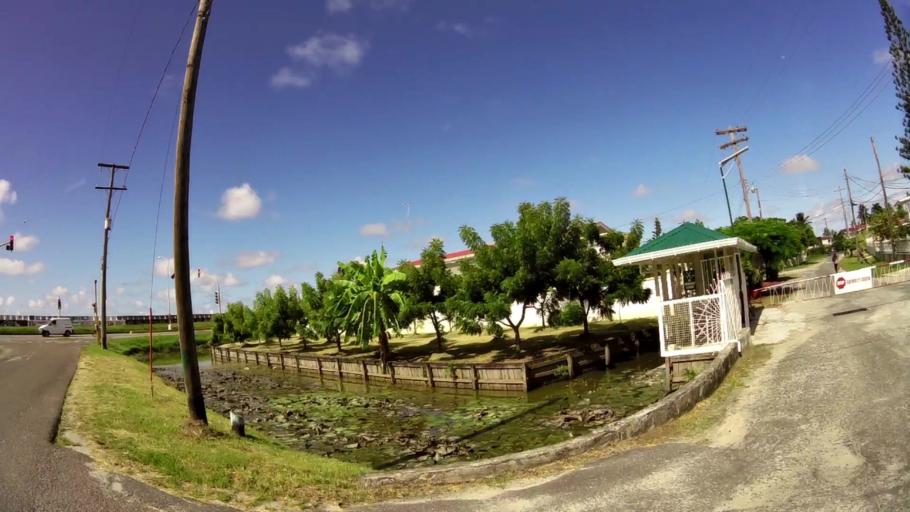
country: GY
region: Demerara-Mahaica
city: Georgetown
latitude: 6.8252
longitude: -58.1295
